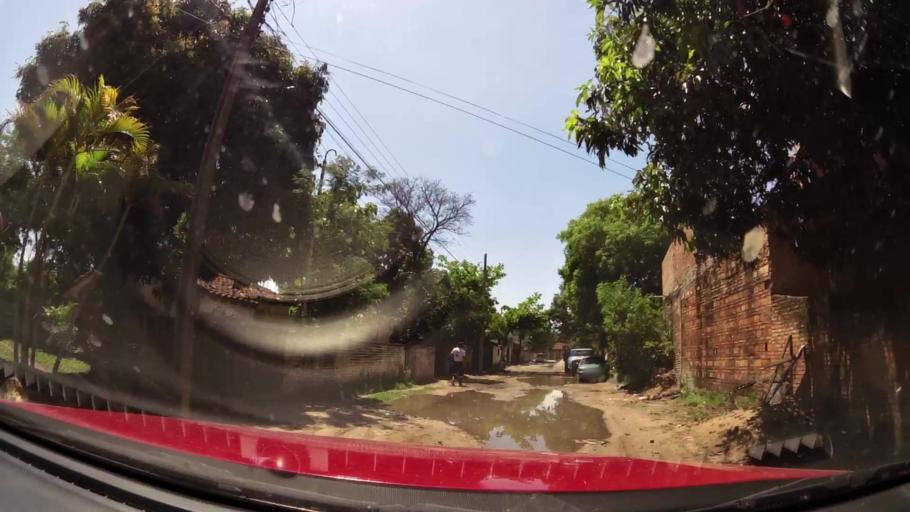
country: PY
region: Central
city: Colonia Mariano Roque Alonso
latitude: -25.2463
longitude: -57.5509
